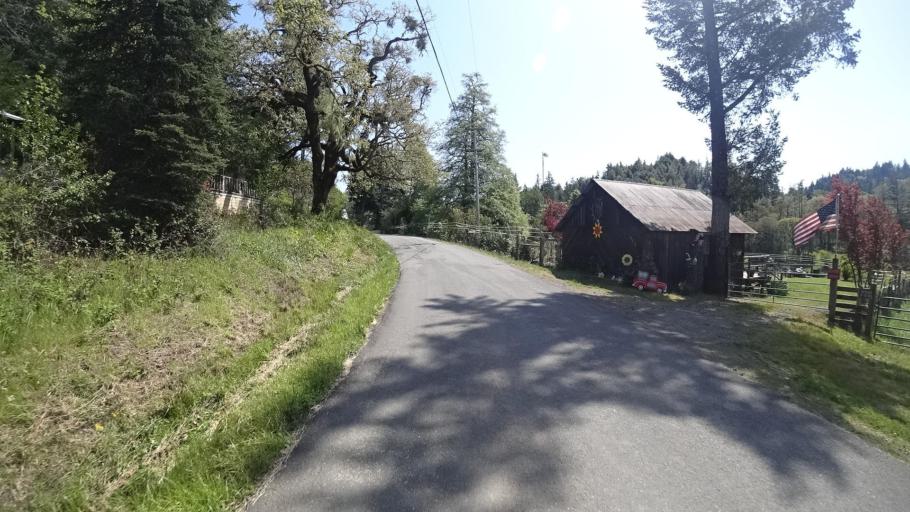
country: US
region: California
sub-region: Humboldt County
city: Redway
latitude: 40.2781
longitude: -123.6406
